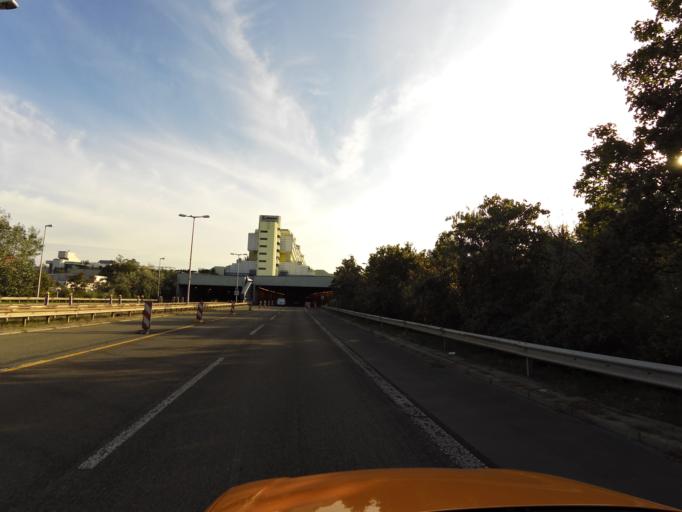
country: DE
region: Berlin
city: Wilmersdorf Bezirk
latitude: 52.4763
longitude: 13.3064
